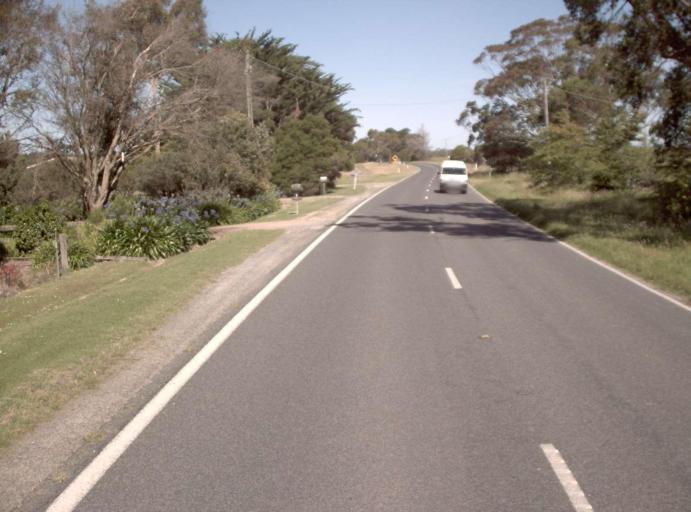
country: AU
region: Victoria
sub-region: Latrobe
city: Morwell
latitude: -38.6694
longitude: 146.3806
